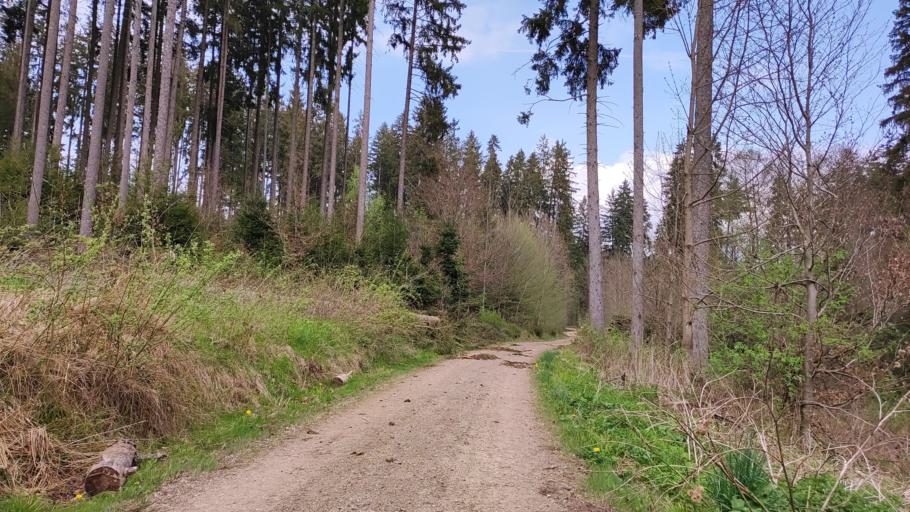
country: DE
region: Bavaria
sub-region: Swabia
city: Holzheim
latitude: 48.4861
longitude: 10.5555
